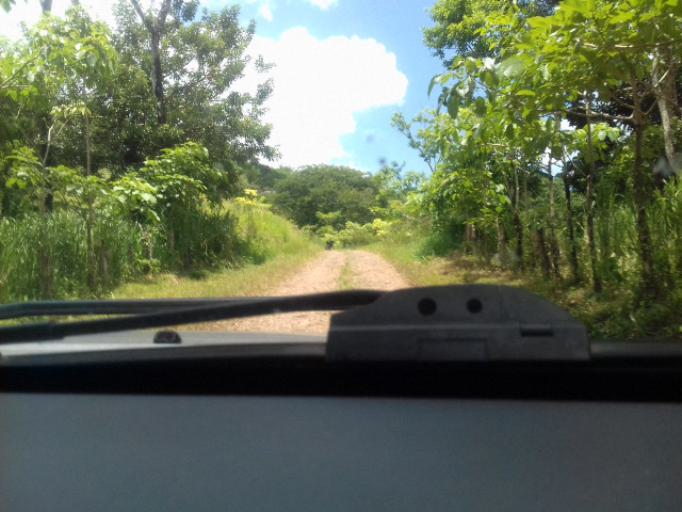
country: NI
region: Matagalpa
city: Matiguas
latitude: 13.0103
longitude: -85.3965
